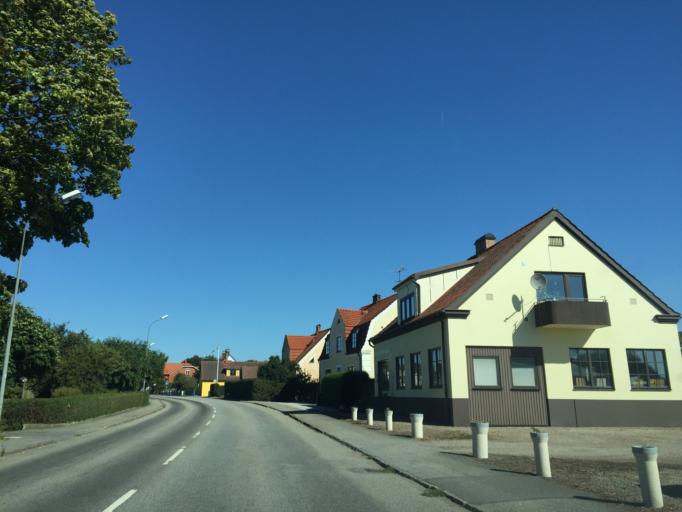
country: SE
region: Skane
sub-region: Ystads Kommun
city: Kopingebro
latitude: 55.4366
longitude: 14.1137
